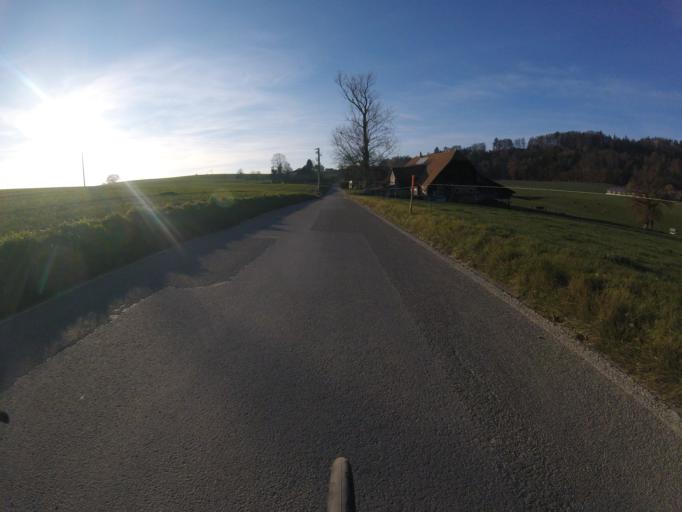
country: CH
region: Bern
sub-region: Bern-Mittelland District
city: Muhleberg
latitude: 46.9382
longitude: 7.2955
